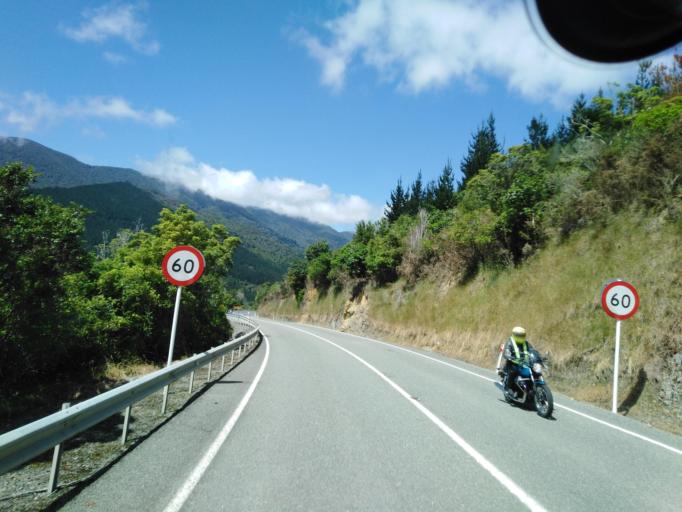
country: NZ
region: Nelson
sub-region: Nelson City
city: Nelson
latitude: -41.2268
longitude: 173.4360
